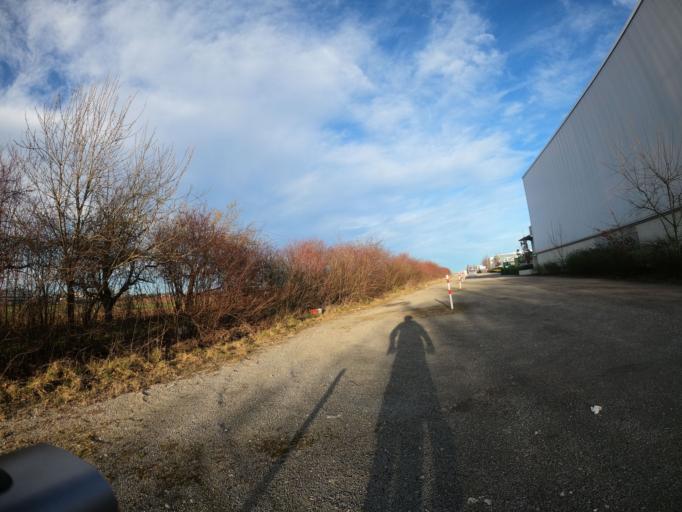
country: DE
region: Baden-Wuerttemberg
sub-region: Regierungsbezirk Stuttgart
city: Denkendorf
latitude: 48.7027
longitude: 9.3093
